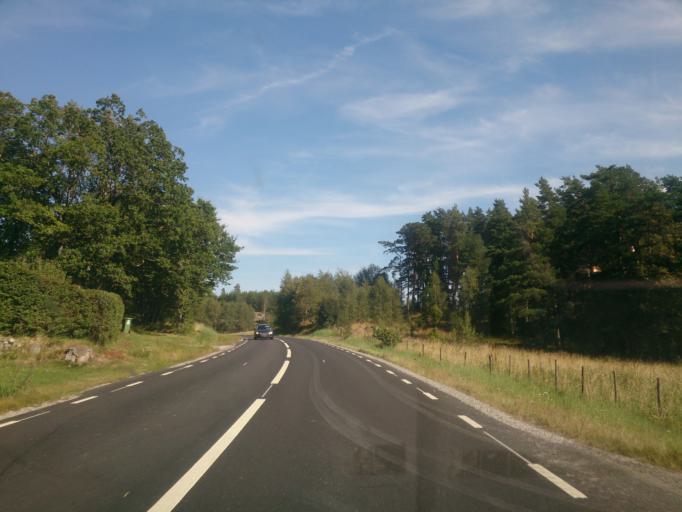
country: SE
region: OEstergoetland
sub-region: Norrkopings Kommun
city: Krokek
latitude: 58.5743
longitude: 16.5076
